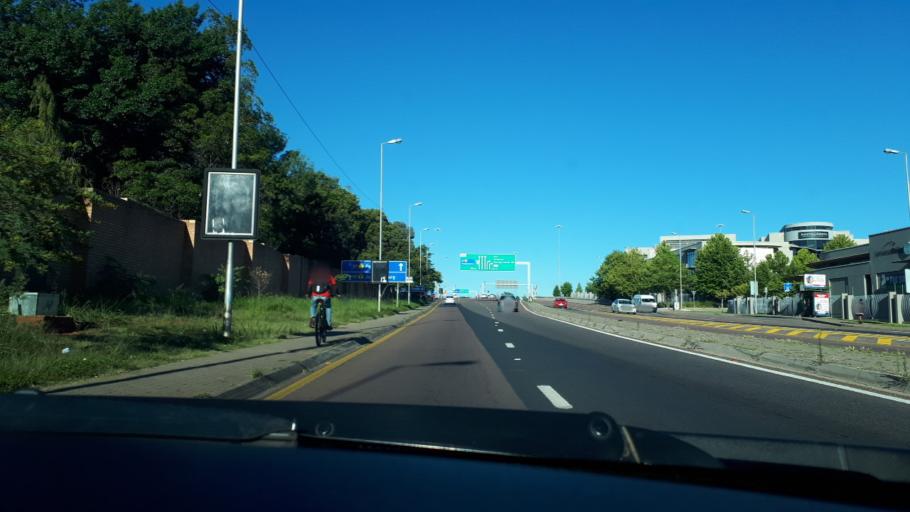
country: ZA
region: Gauteng
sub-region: City of Tshwane Metropolitan Municipality
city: Pretoria
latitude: -25.7667
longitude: 28.2787
